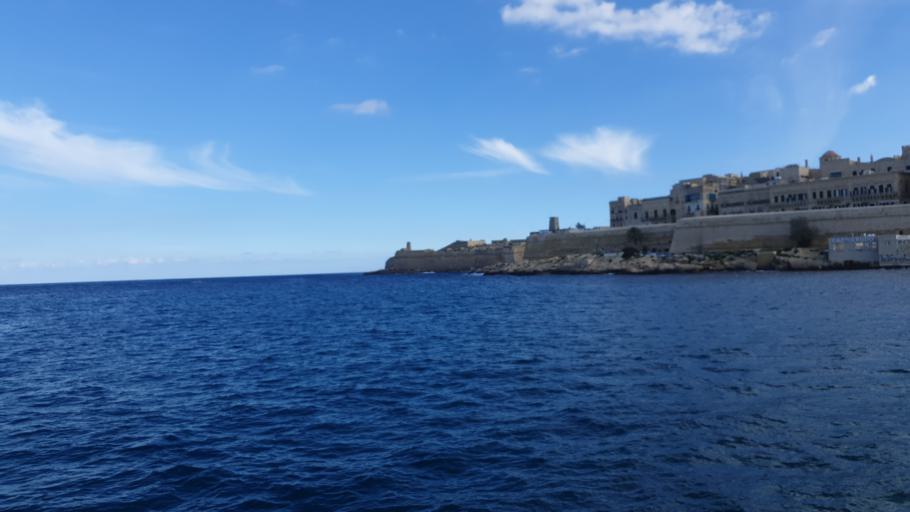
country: MT
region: Il-Belt Valletta
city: Valletta
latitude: 35.9027
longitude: 14.5095
